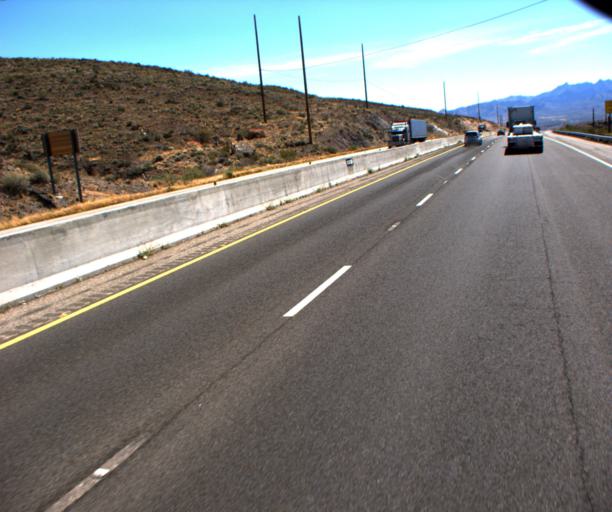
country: US
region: Arizona
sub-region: Mohave County
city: Kingman
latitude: 35.2084
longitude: -114.1017
